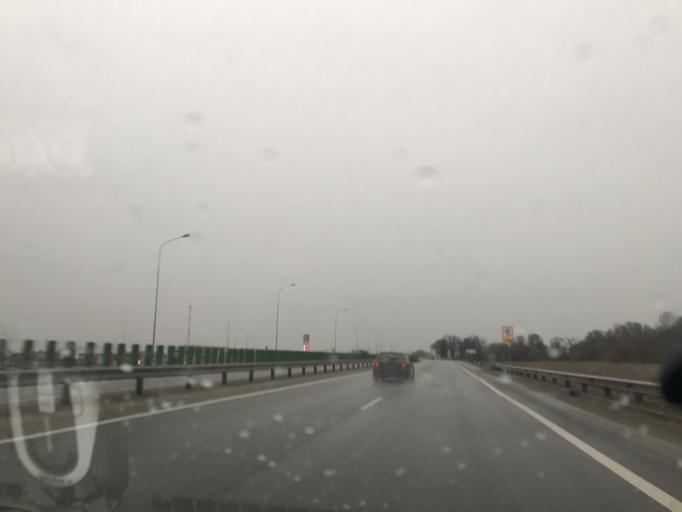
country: RU
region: Krasnodarskiy
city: Pavlovskaya
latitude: 46.2749
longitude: 39.8318
